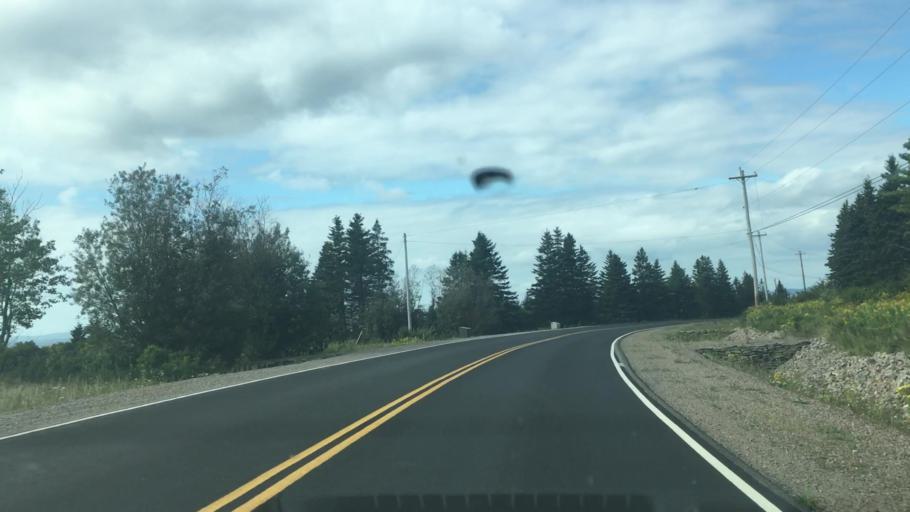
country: CA
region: Nova Scotia
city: Princeville
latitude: 45.7884
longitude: -60.7405
